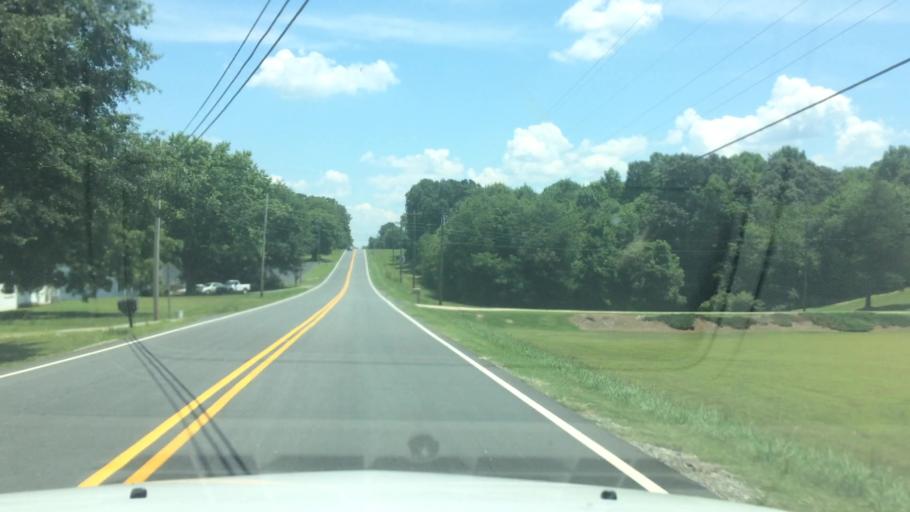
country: US
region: North Carolina
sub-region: Alexander County
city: Taylorsville
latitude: 35.9207
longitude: -81.2405
